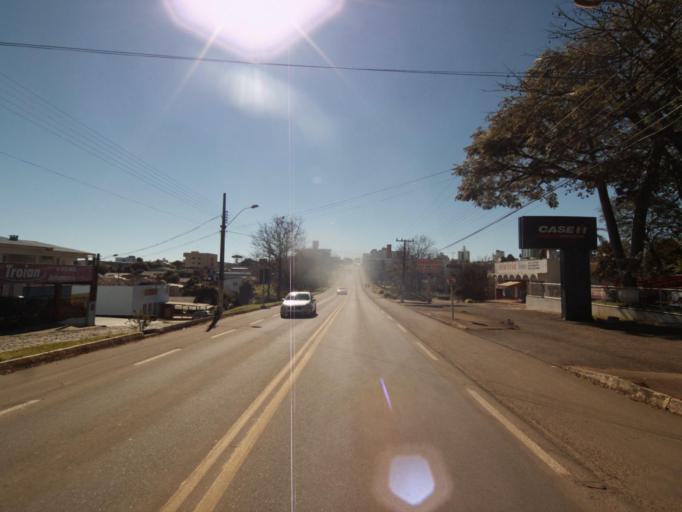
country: AR
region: Misiones
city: Bernardo de Irigoyen
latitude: -26.7364
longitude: -53.5195
